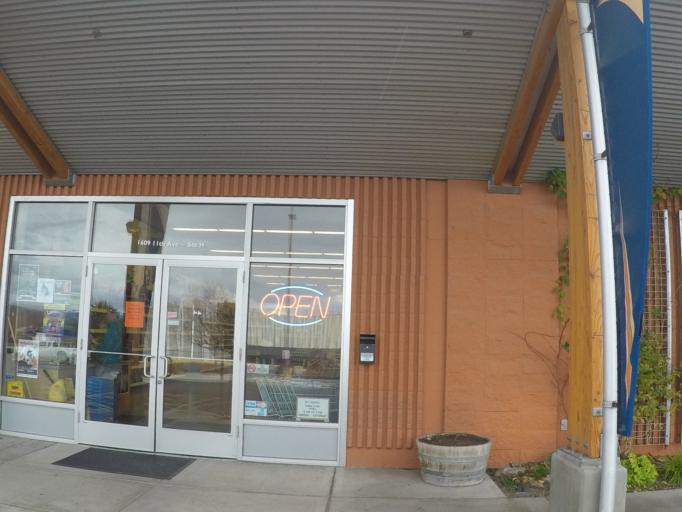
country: US
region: Montana
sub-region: Lewis and Clark County
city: Helena
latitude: 46.5894
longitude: -112.0123
